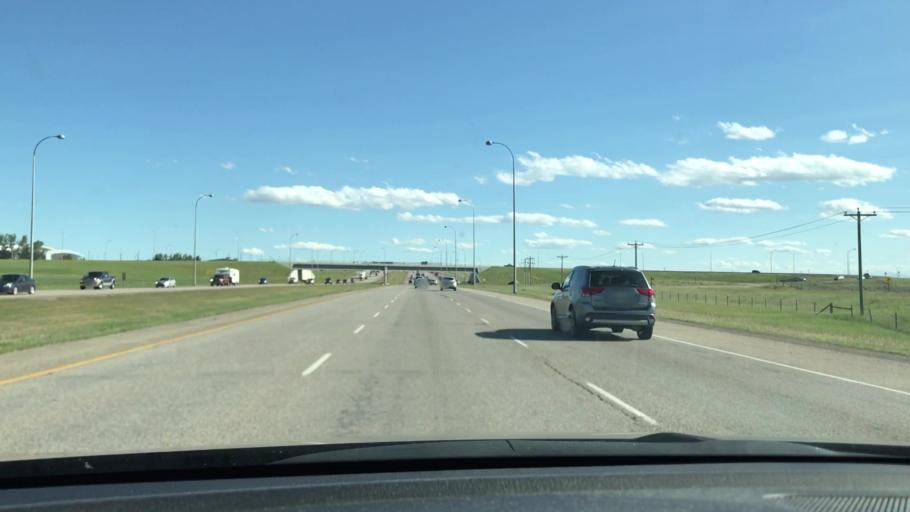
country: CA
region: Alberta
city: Airdrie
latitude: 51.2018
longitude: -114.0017
